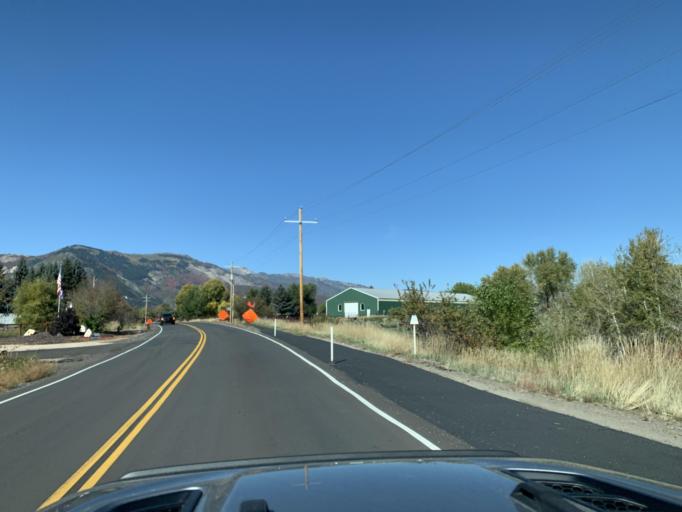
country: US
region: Utah
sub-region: Weber County
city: Wolf Creek
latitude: 41.3125
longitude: -111.8365
